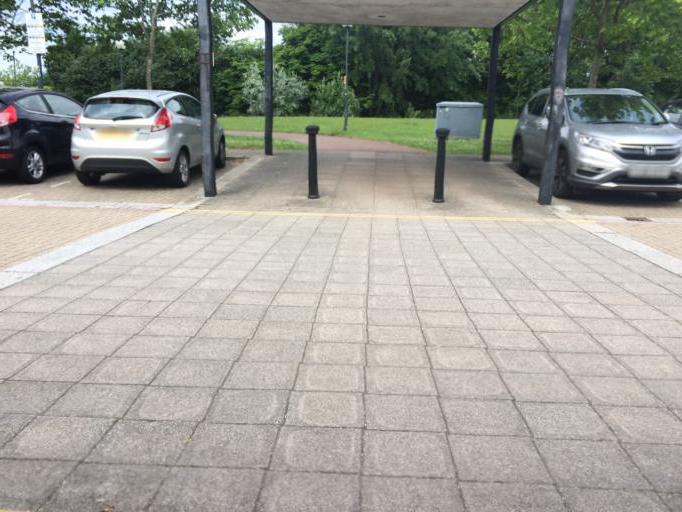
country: GB
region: England
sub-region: Milton Keynes
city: Loughton
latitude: 52.0396
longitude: -0.7726
